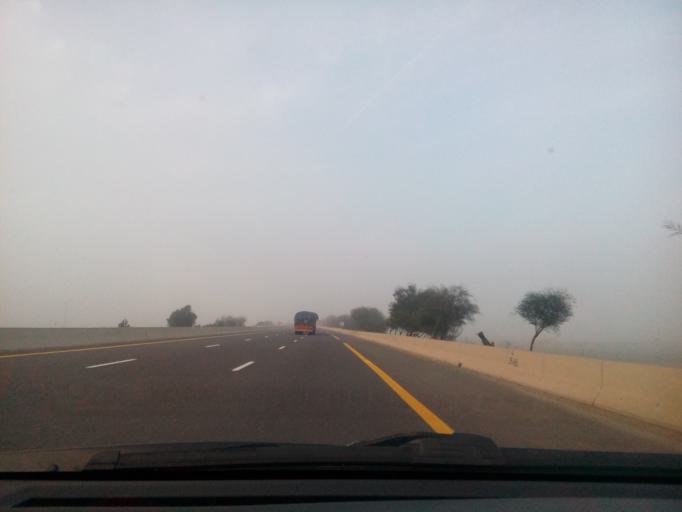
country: DZ
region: Relizane
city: Relizane
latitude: 35.7982
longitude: 0.5086
